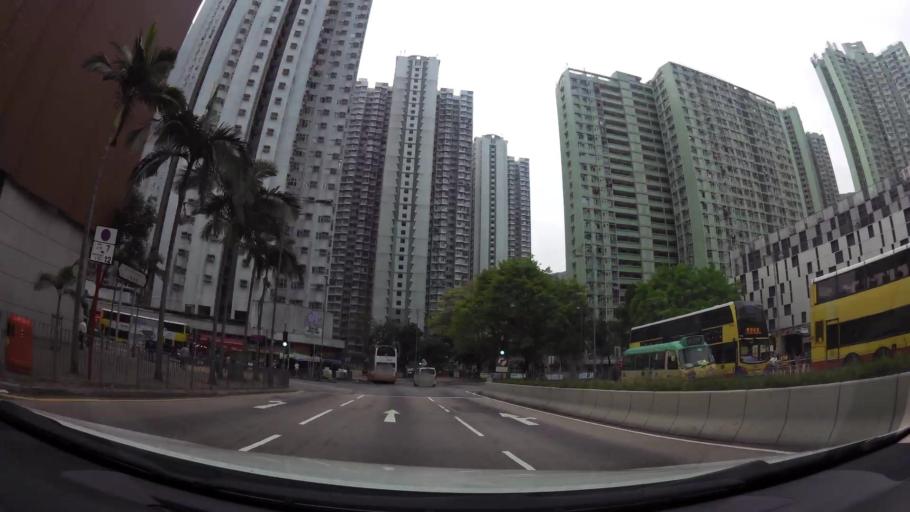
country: HK
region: Wanchai
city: Wan Chai
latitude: 22.2632
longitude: 114.2493
